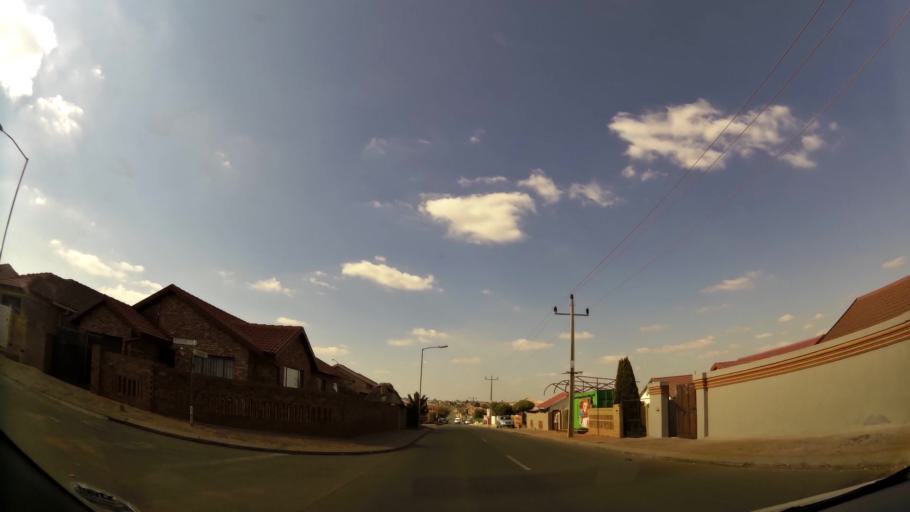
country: ZA
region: Gauteng
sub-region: West Rand District Municipality
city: Krugersdorp
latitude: -26.1650
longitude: 27.7865
